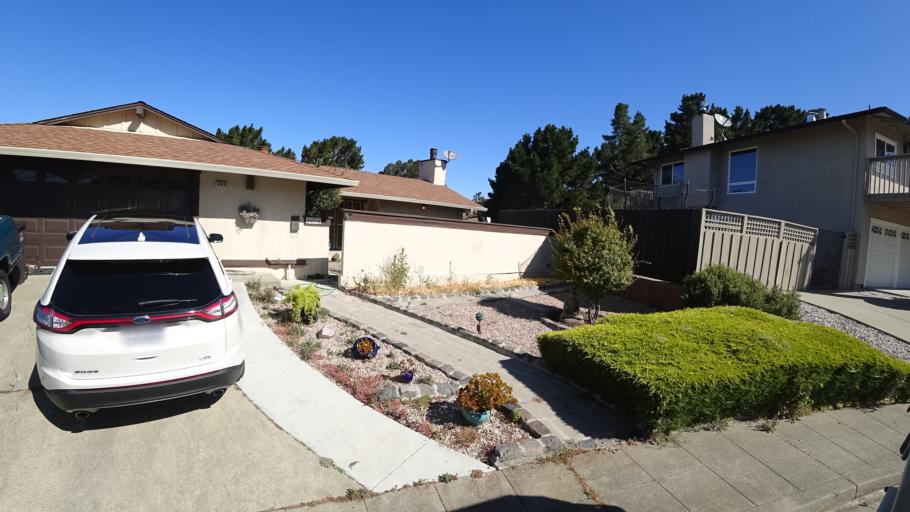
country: US
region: California
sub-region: Alameda County
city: Fairview
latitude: 37.6521
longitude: -122.0316
